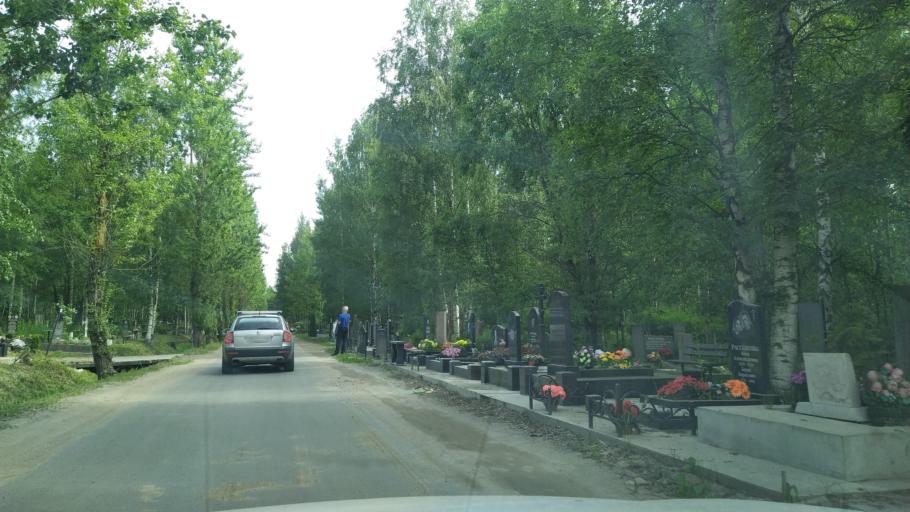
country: RU
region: St.-Petersburg
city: Dachnoye
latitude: 59.7682
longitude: 30.2635
